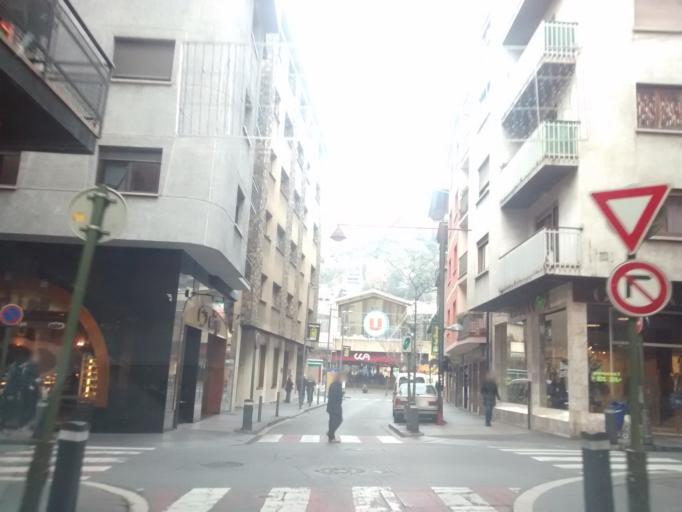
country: AD
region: Escaldes-Engordany
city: les Escaldes
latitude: 42.5069
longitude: 1.5312
